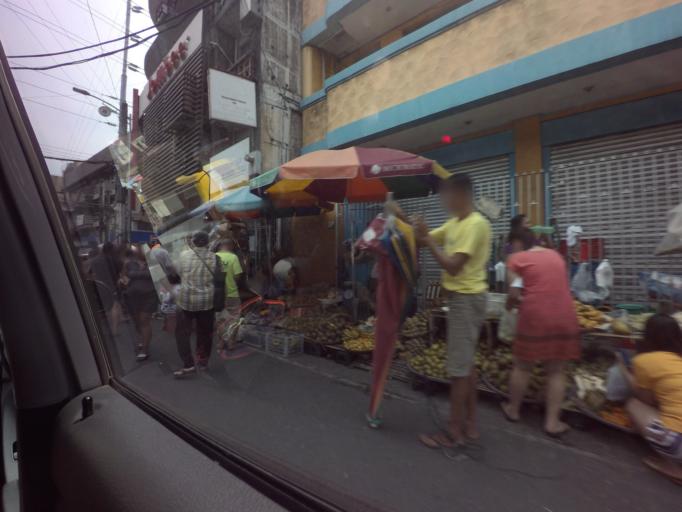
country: PH
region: Metro Manila
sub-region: City of Manila
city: Quiapo
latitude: 14.5717
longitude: 120.9959
